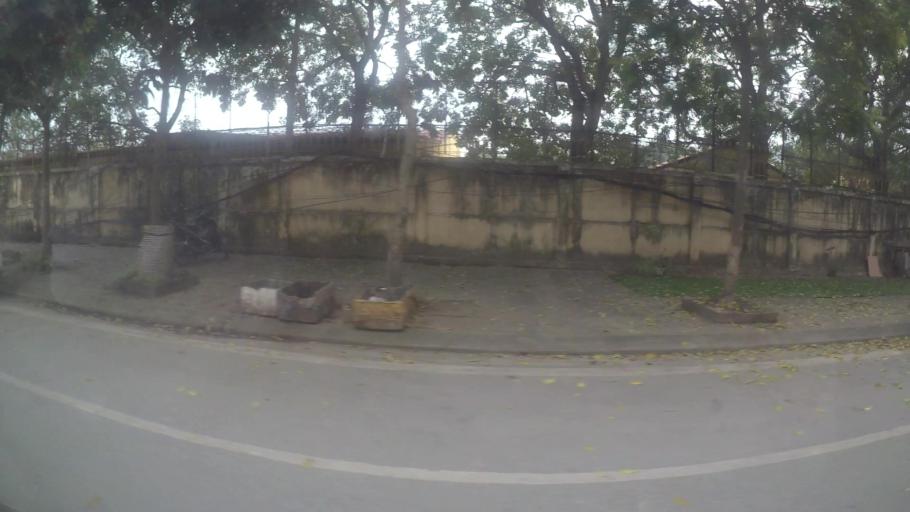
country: VN
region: Ha Noi
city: Cau Dien
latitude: 21.0415
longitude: 105.7531
